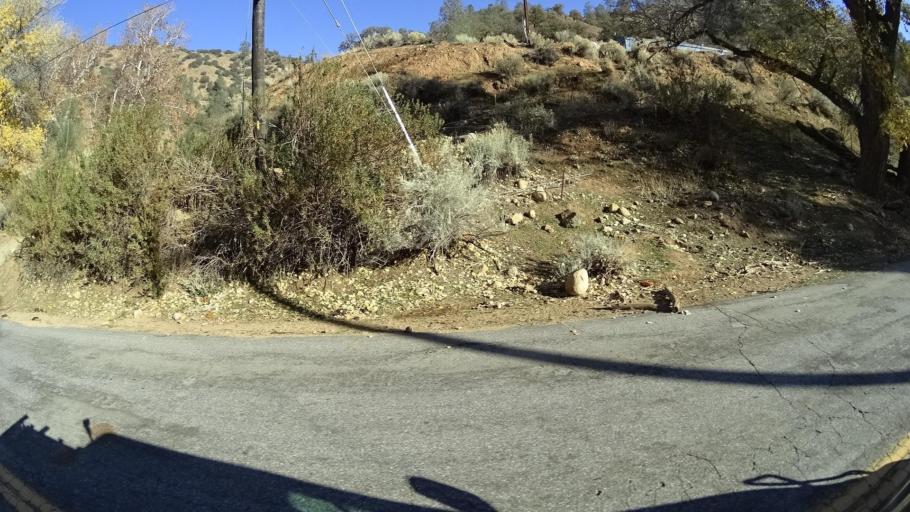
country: US
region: California
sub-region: Kern County
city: Golden Hills
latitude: 35.3044
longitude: -118.4605
